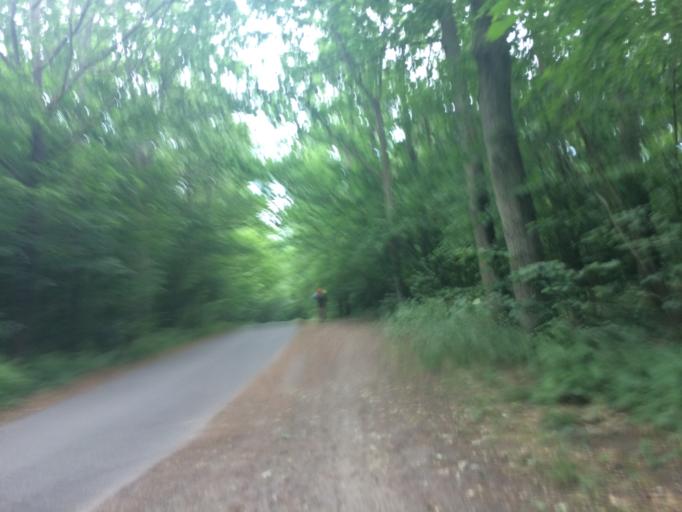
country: DK
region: Capital Region
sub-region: Bornholm Kommune
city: Ronne
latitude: 55.1428
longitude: 14.7134
